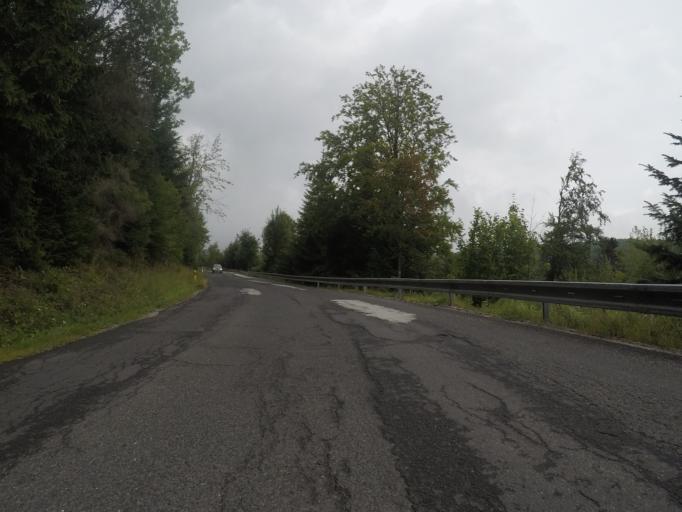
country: SK
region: Kosicky
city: Spisska Nova Ves
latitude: 48.8640
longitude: 20.5283
